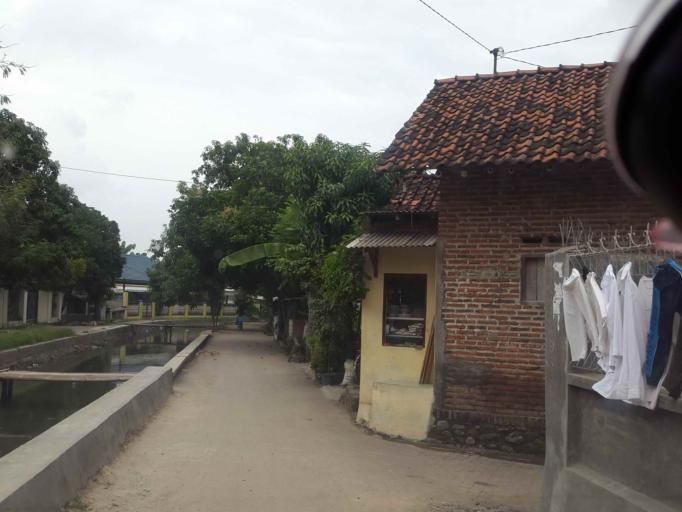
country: ID
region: Central Java
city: Dukuhturi
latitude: -6.8810
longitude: 109.0885
